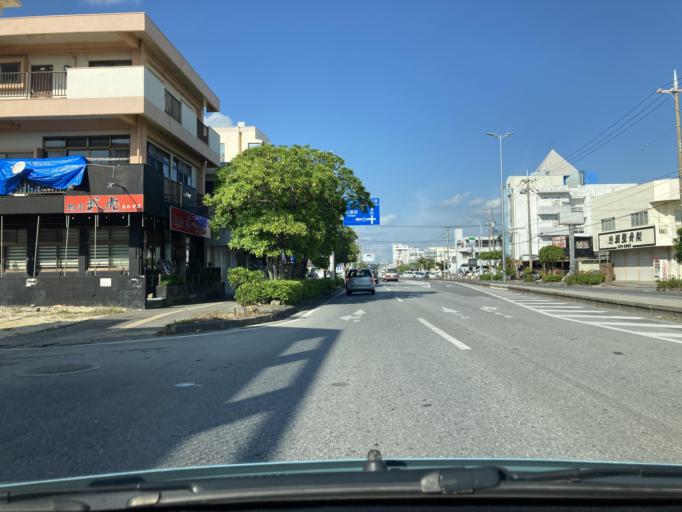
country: JP
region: Okinawa
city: Okinawa
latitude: 26.3154
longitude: 127.8299
